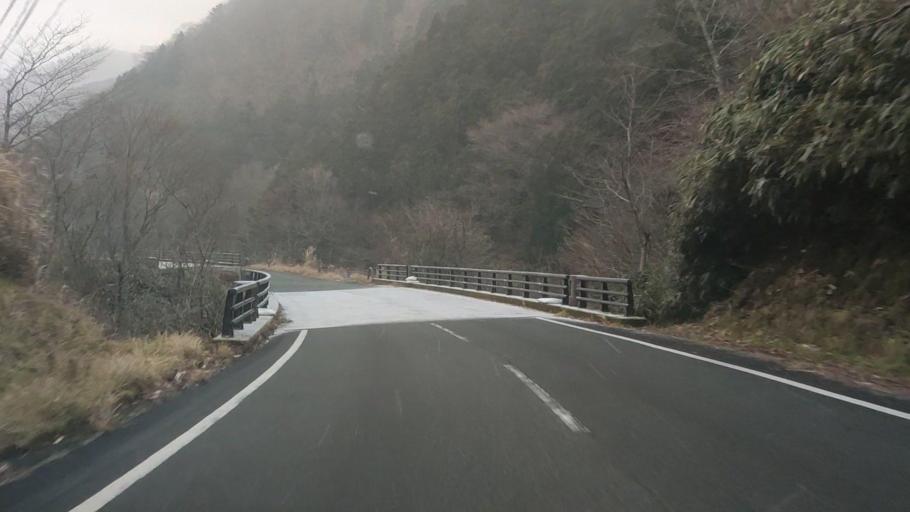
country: JP
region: Kumamoto
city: Matsubase
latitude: 32.5639
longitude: 130.9134
